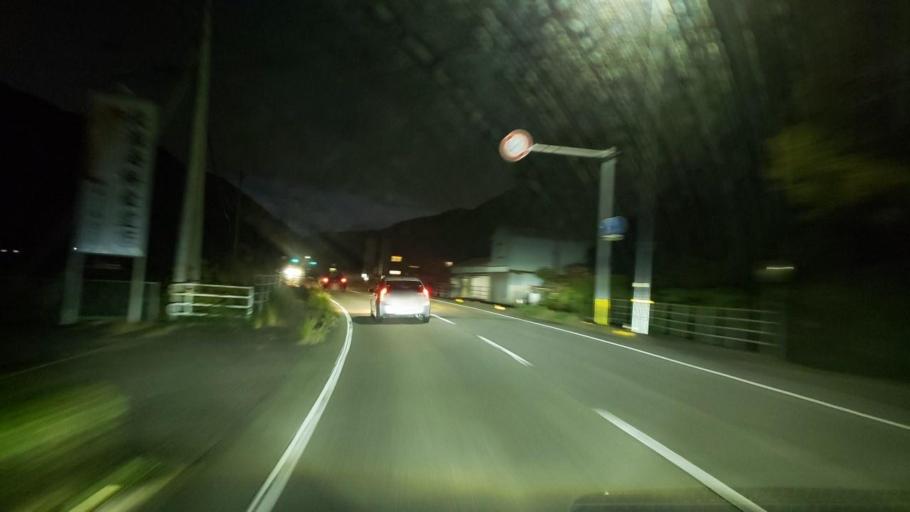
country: JP
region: Tokushima
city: Narutocho-mitsuishi
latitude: 34.2155
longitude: 134.5591
